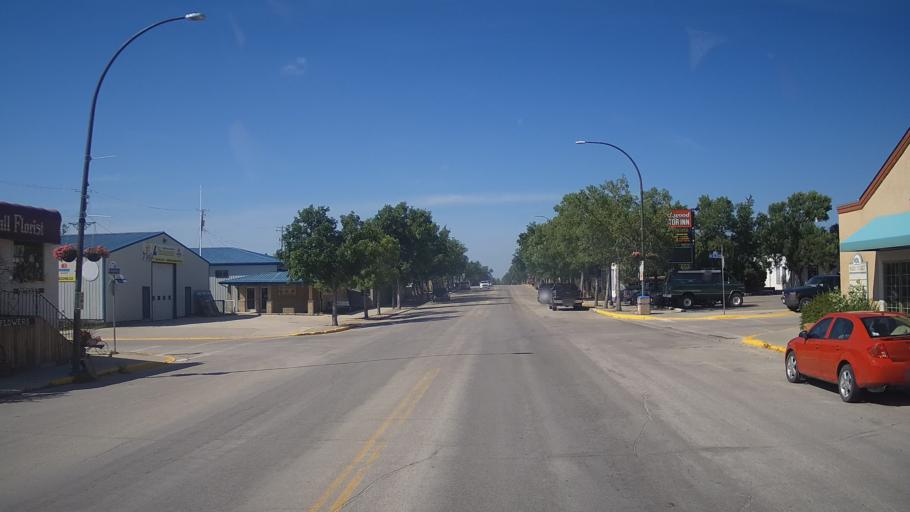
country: CA
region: Manitoba
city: Stonewall
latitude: 50.1330
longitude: -97.3266
